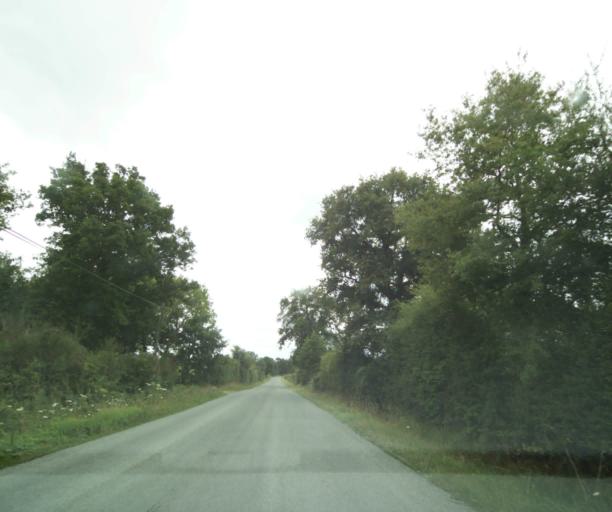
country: FR
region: Pays de la Loire
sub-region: Departement de Maine-et-Loire
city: Durtal
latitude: 47.6914
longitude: -0.2615
